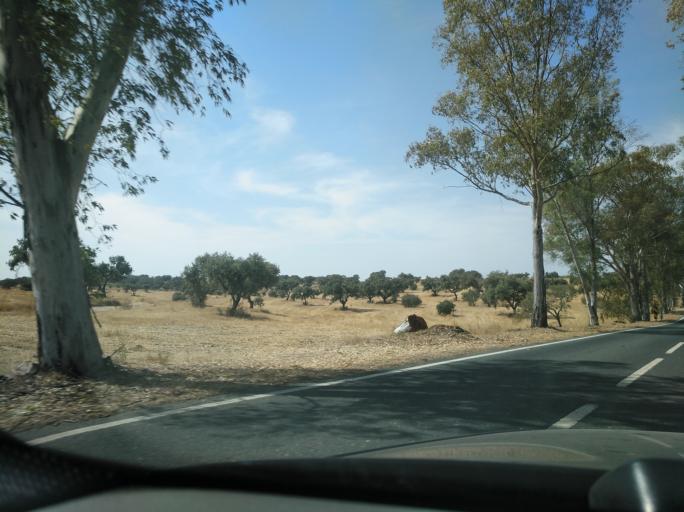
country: PT
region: Beja
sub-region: Mertola
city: Mertola
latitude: 37.7244
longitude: -7.7636
